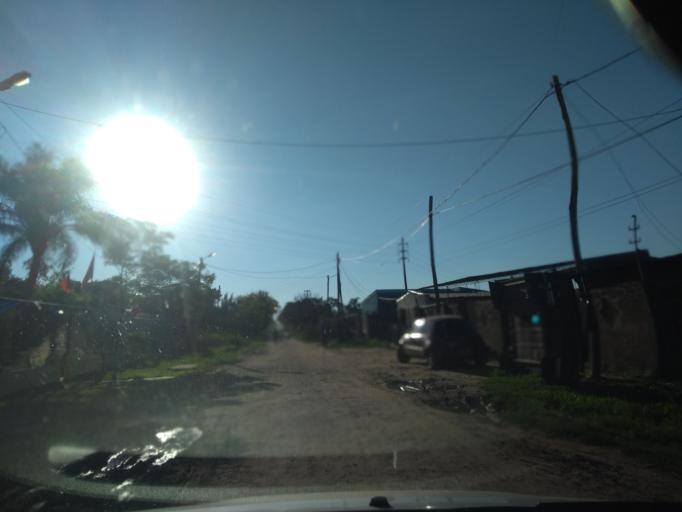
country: AR
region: Chaco
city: Barranqueras
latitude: -27.4777
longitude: -58.9261
